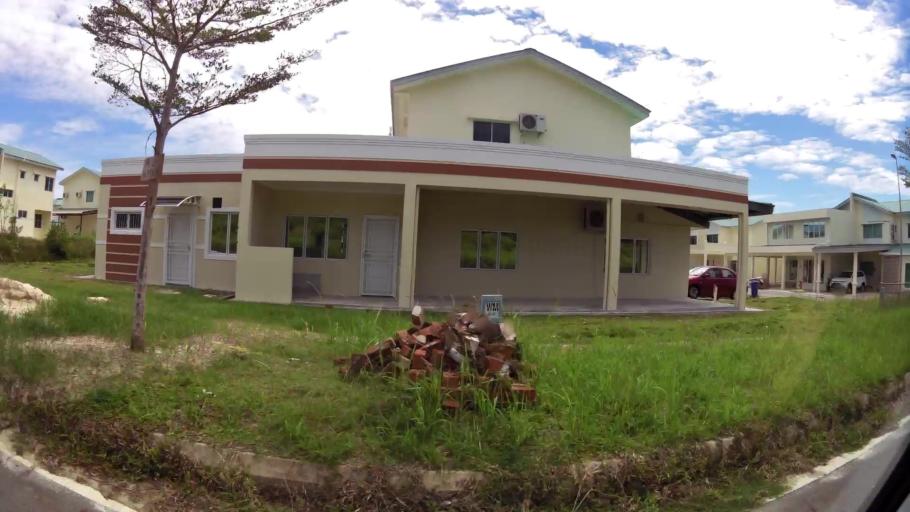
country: BN
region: Brunei and Muara
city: Bandar Seri Begawan
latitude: 4.9715
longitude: 115.0129
